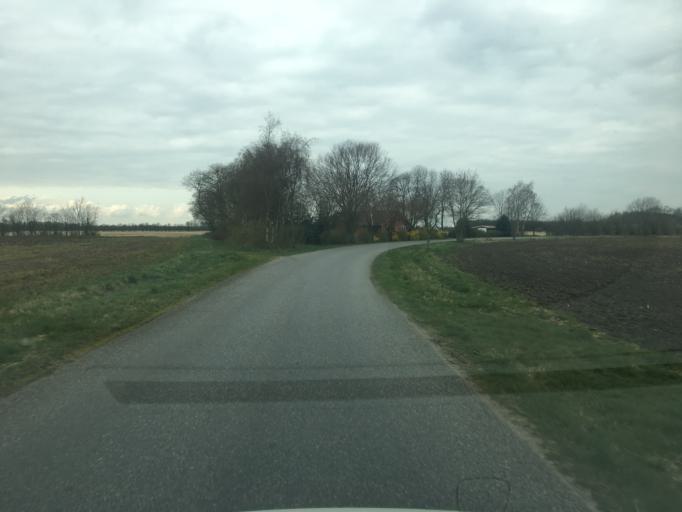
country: DK
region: South Denmark
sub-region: Tonder Kommune
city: Toftlund
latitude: 55.0455
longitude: 9.1351
